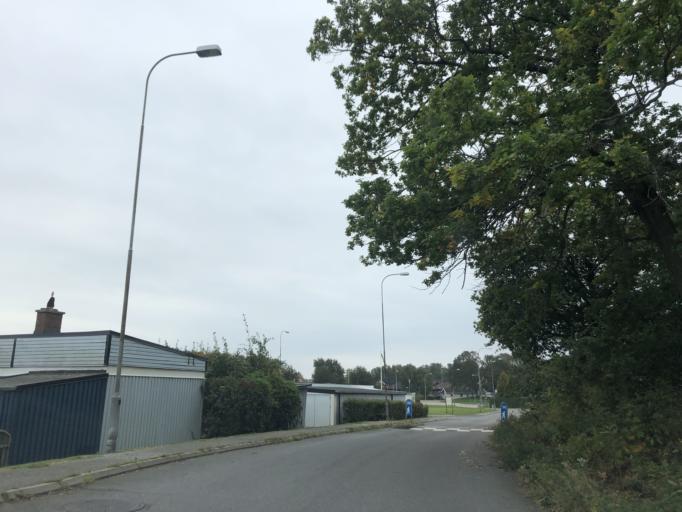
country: SE
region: Vaestra Goetaland
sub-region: Goteborg
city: Majorna
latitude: 57.6569
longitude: 11.8750
